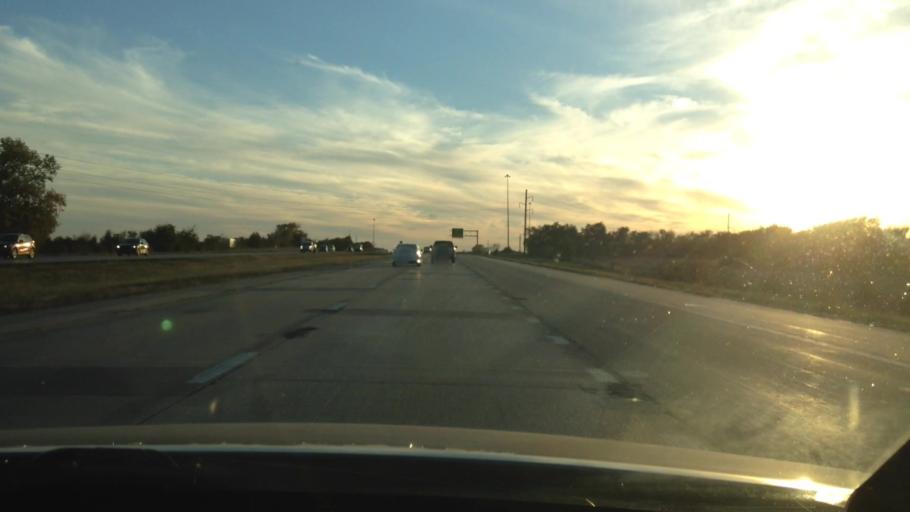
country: US
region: Kansas
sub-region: Johnson County
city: Olathe
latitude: 38.8345
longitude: -94.8455
